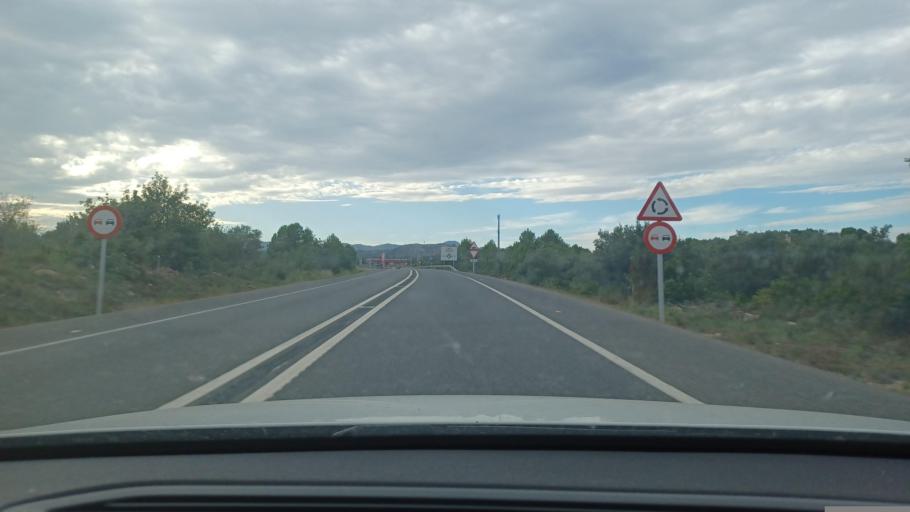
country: ES
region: Catalonia
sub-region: Provincia de Tarragona
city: l'Ametlla de Mar
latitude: 40.8960
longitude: 0.7545
